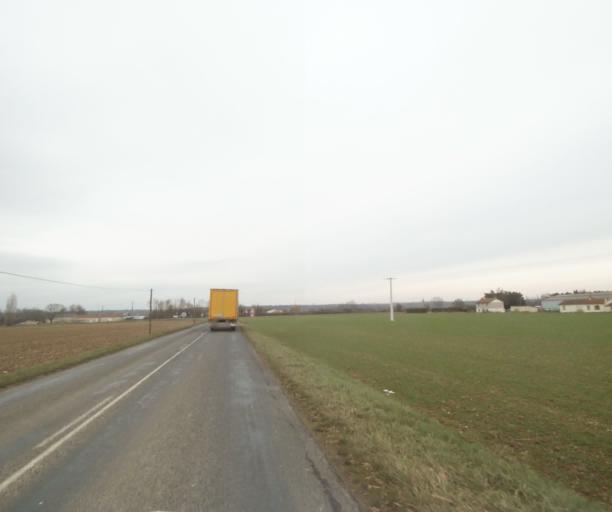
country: FR
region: Champagne-Ardenne
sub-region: Departement de la Haute-Marne
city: Villiers-en-Lieu
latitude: 48.6545
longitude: 4.9086
